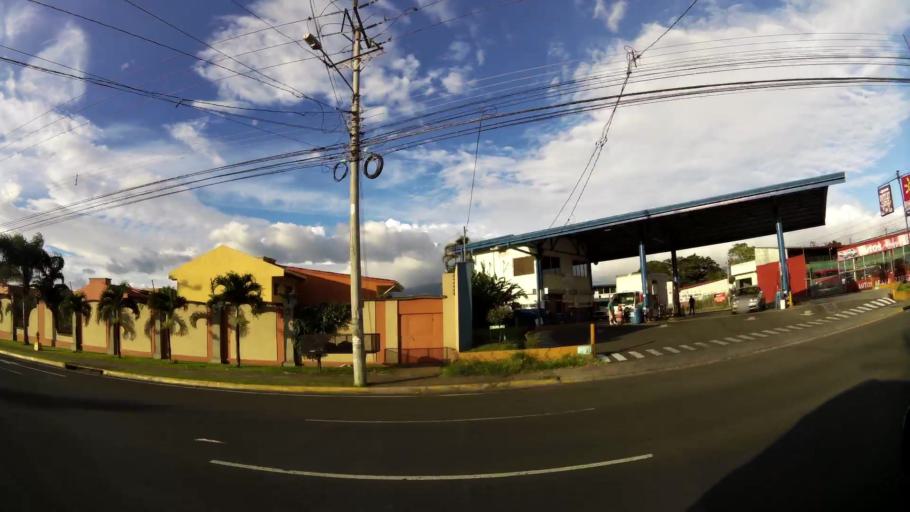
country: CR
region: Heredia
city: Llorente
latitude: 10.0019
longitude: -84.1571
